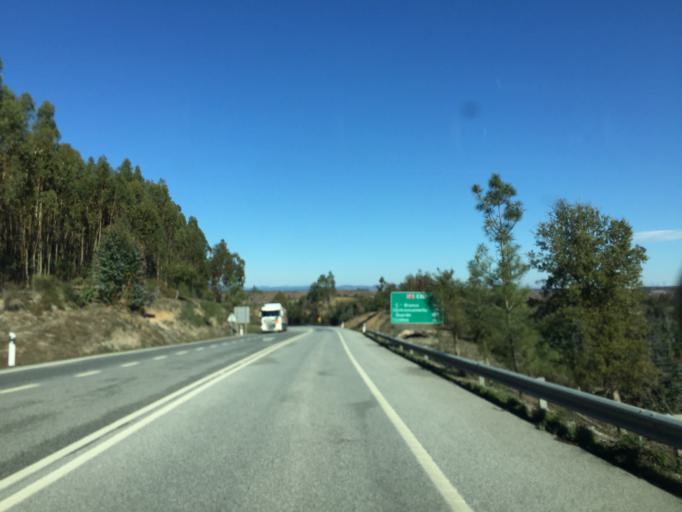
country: PT
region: Portalegre
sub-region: Nisa
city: Nisa
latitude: 39.5002
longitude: -7.7685
